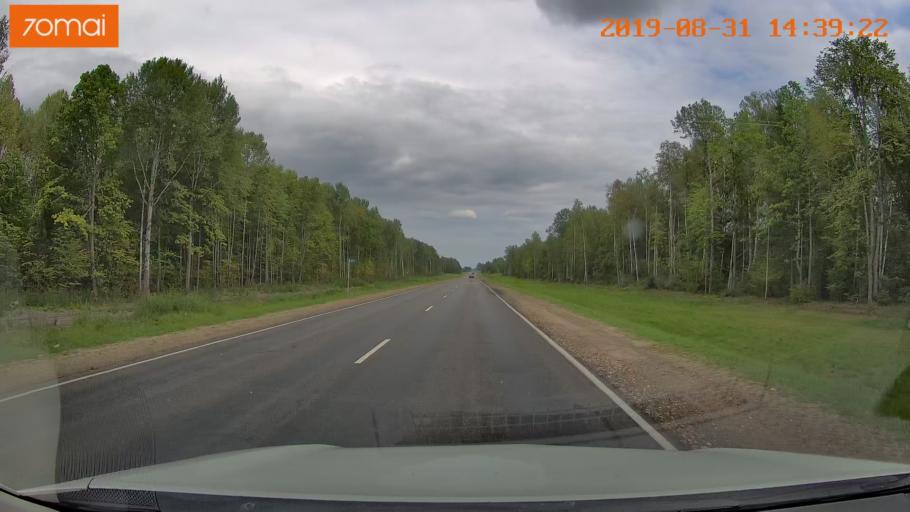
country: RU
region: Smolensk
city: Yekimovichi
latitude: 54.1911
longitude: 33.5509
